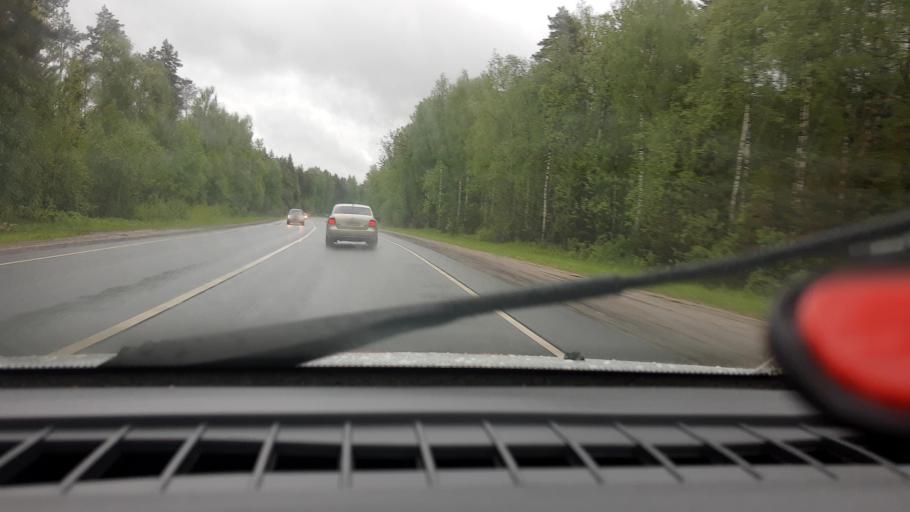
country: RU
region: Nizjnij Novgorod
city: Linda
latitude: 56.6372
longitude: 44.1046
